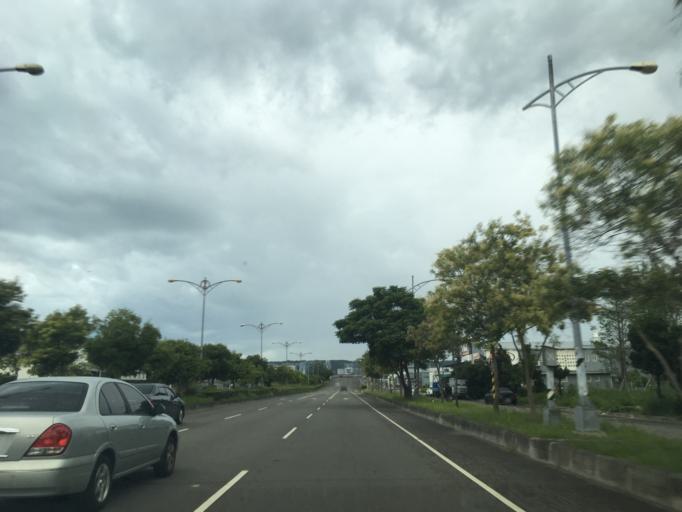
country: TW
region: Taiwan
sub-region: Taichung City
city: Taichung
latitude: 24.2024
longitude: 120.6416
